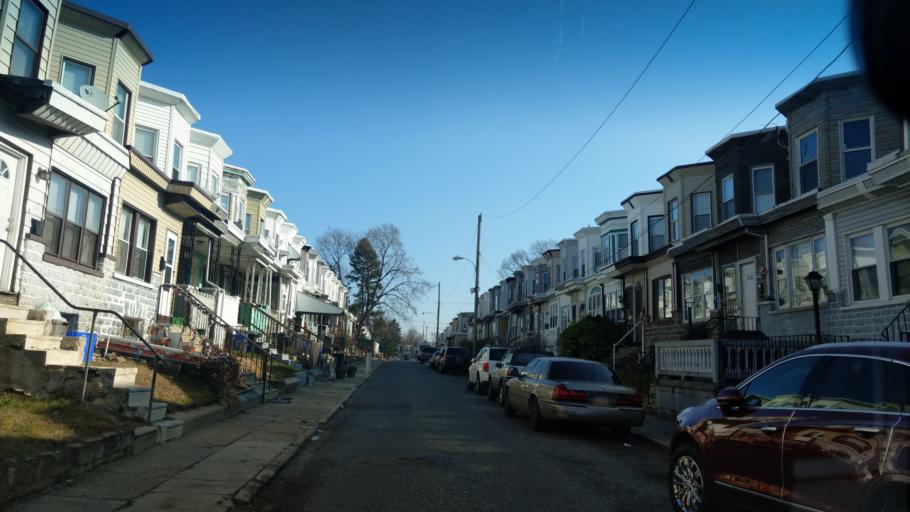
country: US
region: Pennsylvania
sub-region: Montgomery County
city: Rockledge
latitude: 40.0313
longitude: -75.1309
